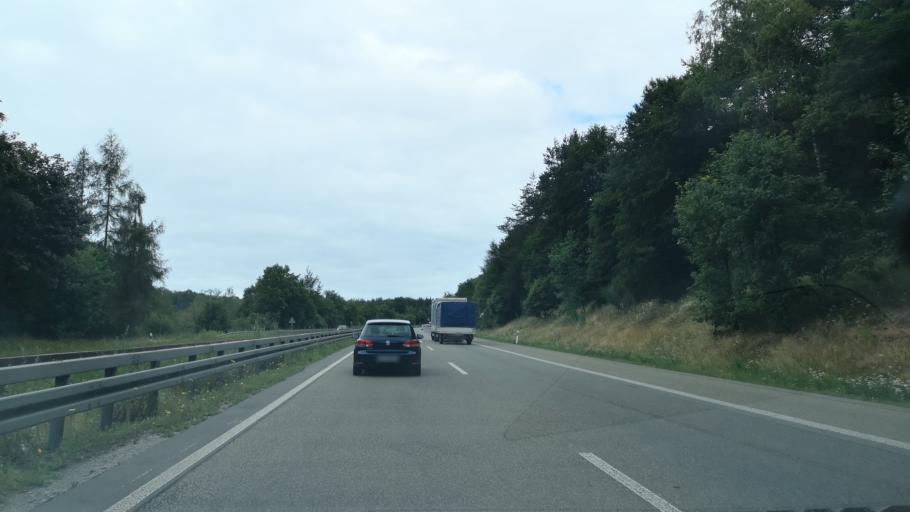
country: DE
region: Bavaria
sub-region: Regierungsbezirk Unterfranken
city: Motten
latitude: 50.3587
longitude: 9.7355
